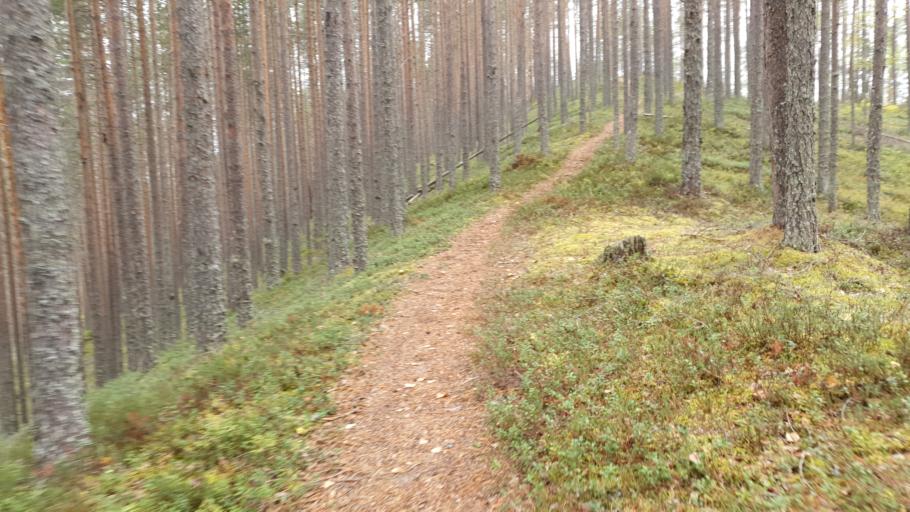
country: FI
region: Kainuu
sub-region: Kehys-Kainuu
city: Kuhmo
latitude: 64.2933
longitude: 29.3468
